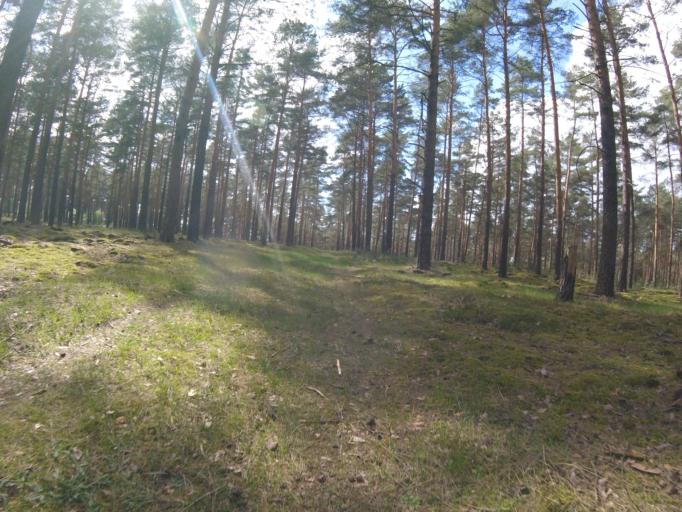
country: DE
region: Brandenburg
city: Schwerin
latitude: 52.1967
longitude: 13.5941
